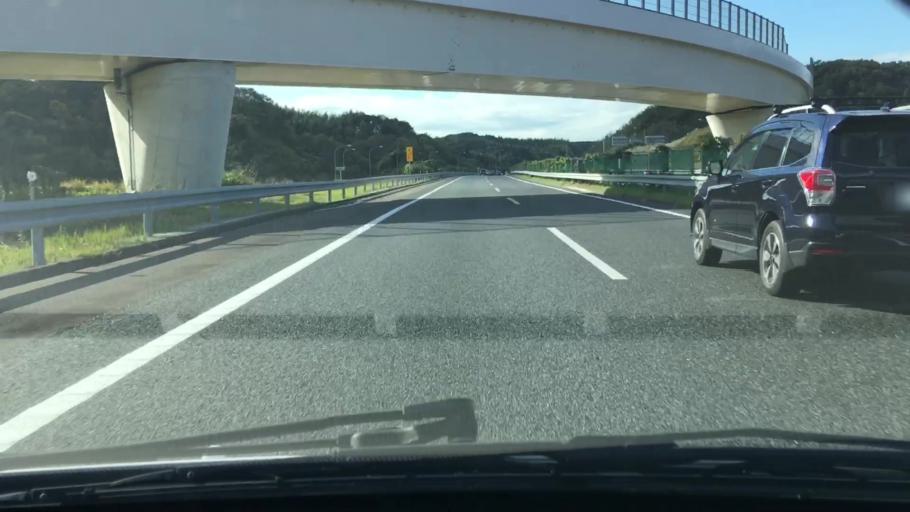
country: JP
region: Chiba
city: Kisarazu
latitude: 35.3757
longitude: 139.9791
